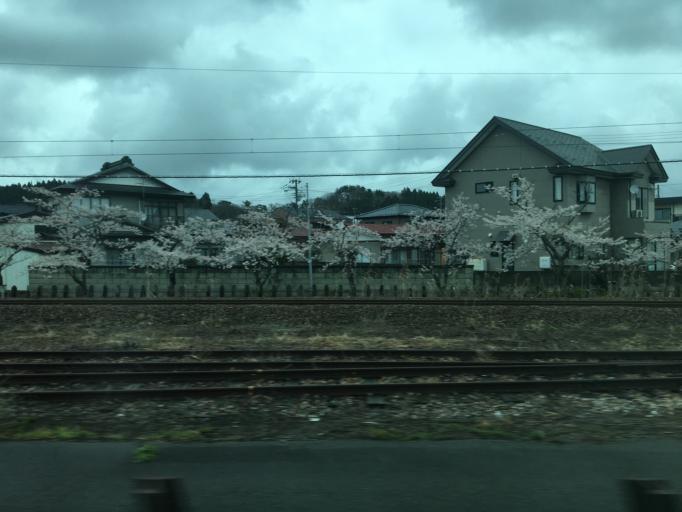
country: JP
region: Akita
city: Akita
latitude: 39.7335
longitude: 140.1206
